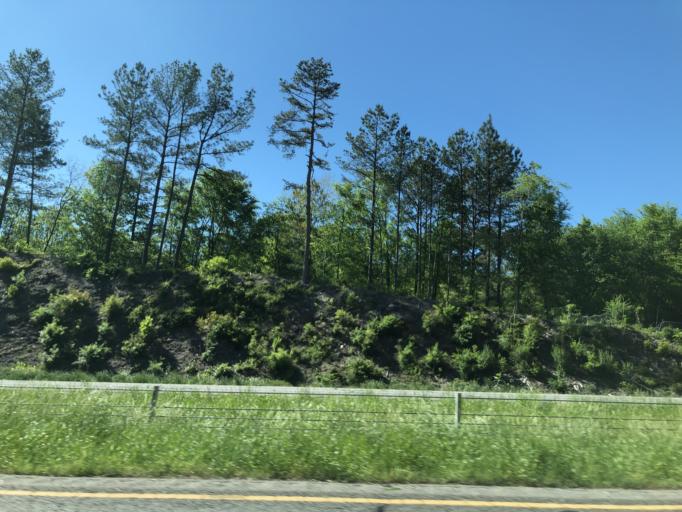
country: US
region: Georgia
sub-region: Clarke County
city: Country Club Estates
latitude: 33.9580
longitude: -83.4351
